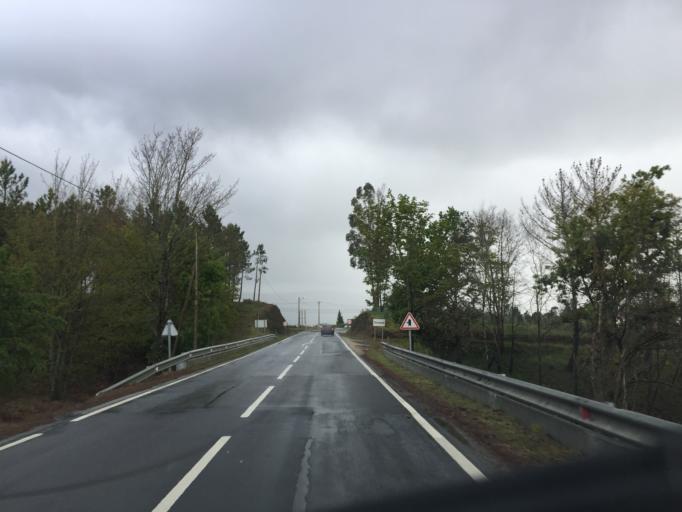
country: PT
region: Guarda
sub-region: Seia
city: Seia
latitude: 40.3884
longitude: -7.7517
